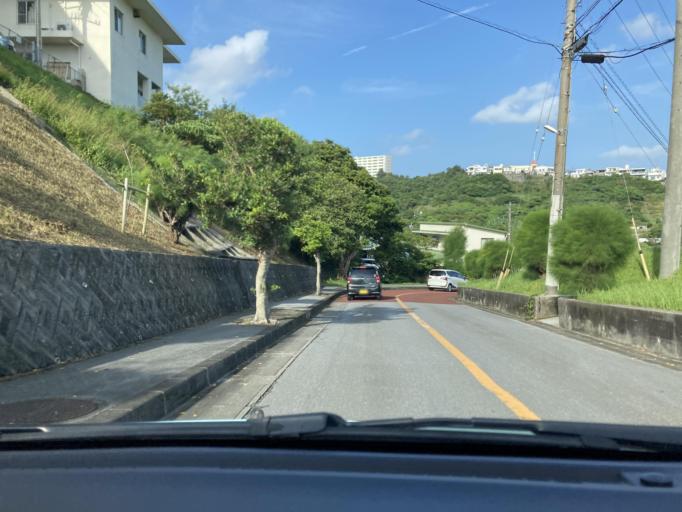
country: JP
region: Okinawa
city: Ginowan
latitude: 26.2293
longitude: 127.7407
